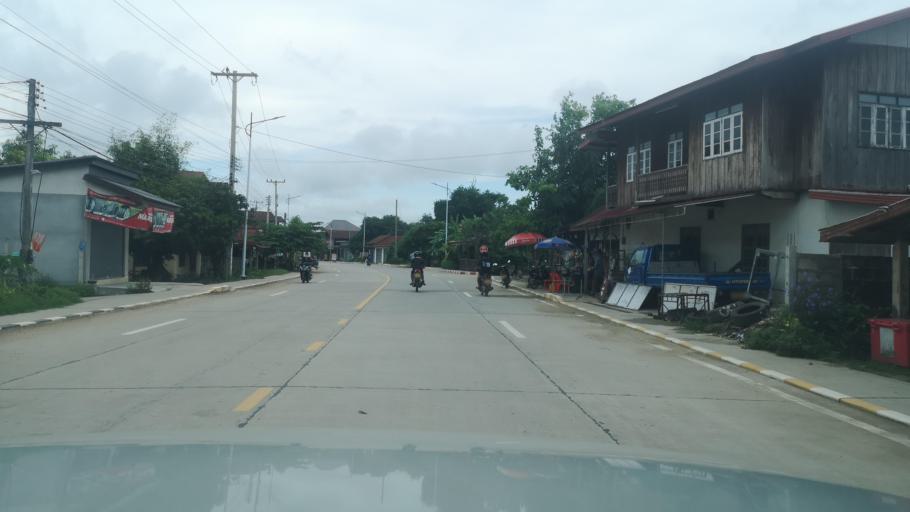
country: TH
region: Nong Khai
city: Tha Bo
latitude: 17.8271
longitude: 102.6531
